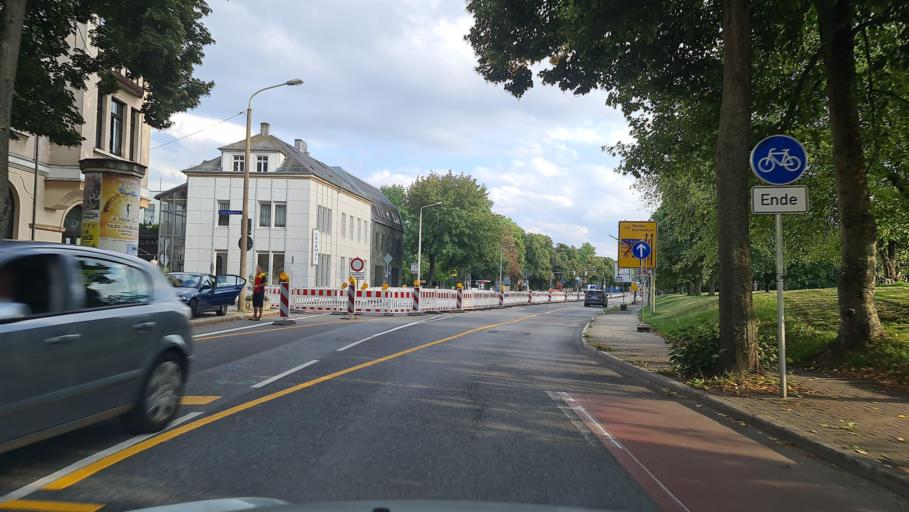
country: DE
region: Saxony
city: Zwickau
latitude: 50.7268
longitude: 12.4852
